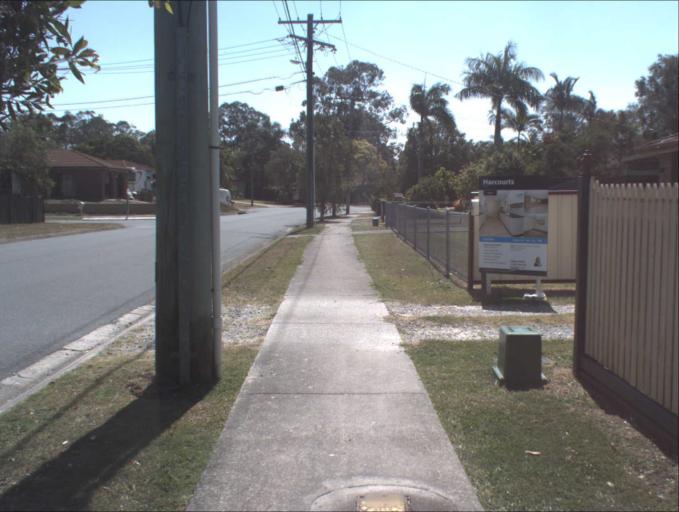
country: AU
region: Queensland
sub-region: Logan
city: Beenleigh
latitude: -27.6863
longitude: 153.1847
